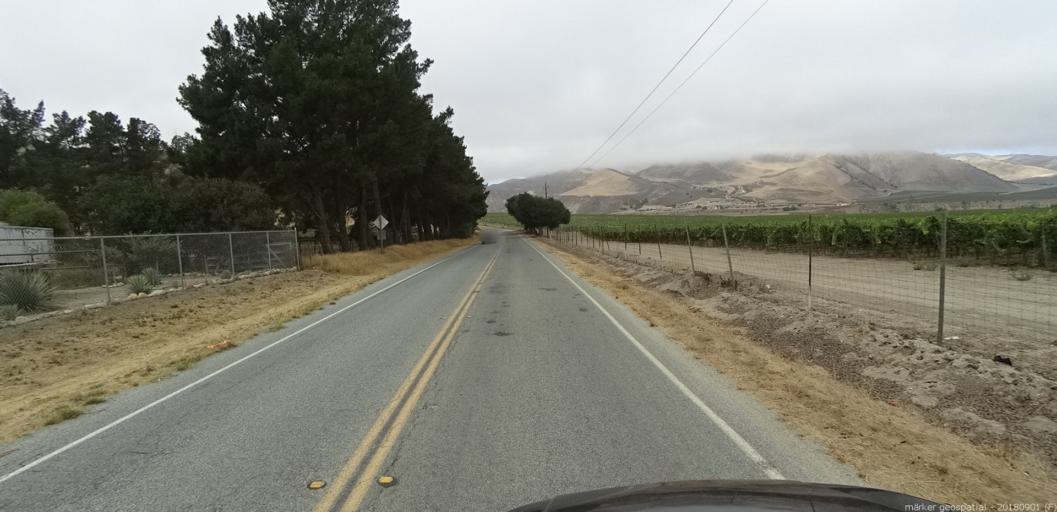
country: US
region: California
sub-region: Monterey County
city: Greenfield
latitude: 36.2805
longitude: -121.3041
